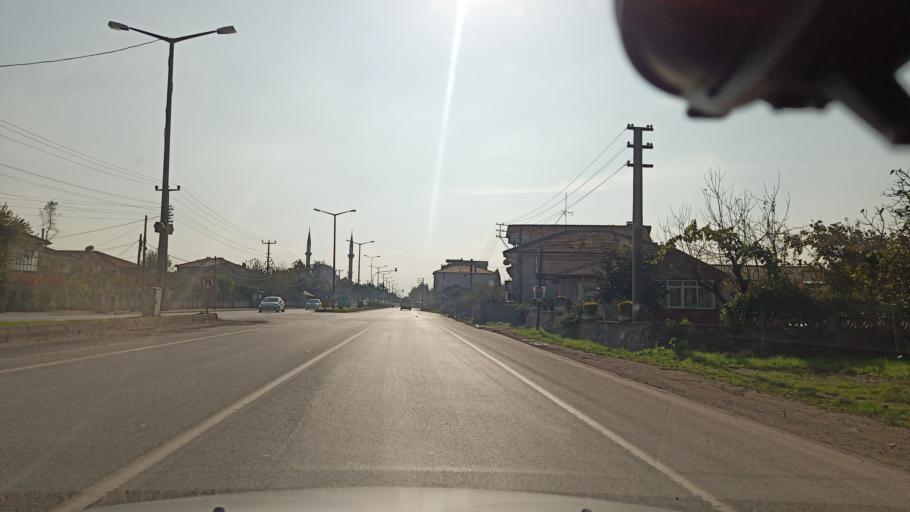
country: TR
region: Sakarya
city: Adapazari
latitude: 40.8118
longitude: 30.4050
